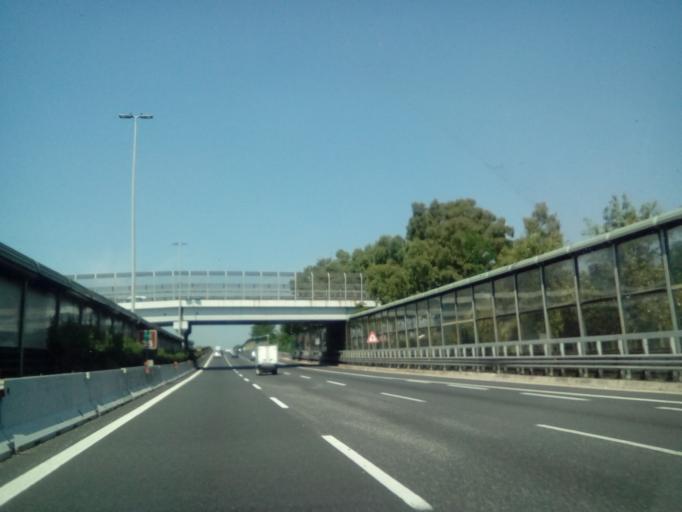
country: IT
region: Latium
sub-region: Citta metropolitana di Roma Capitale
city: Vitinia
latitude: 41.8015
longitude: 12.4488
